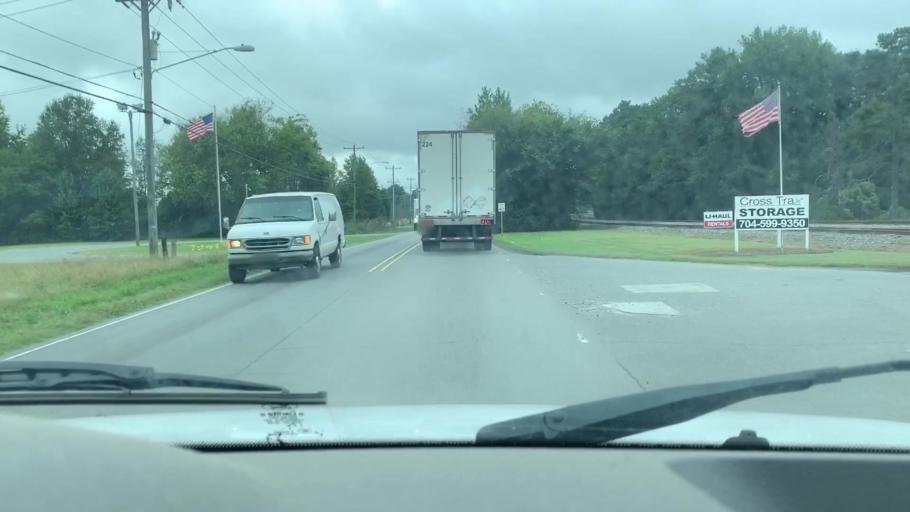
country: US
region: North Carolina
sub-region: Mecklenburg County
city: Huntersville
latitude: 35.3498
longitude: -80.8232
